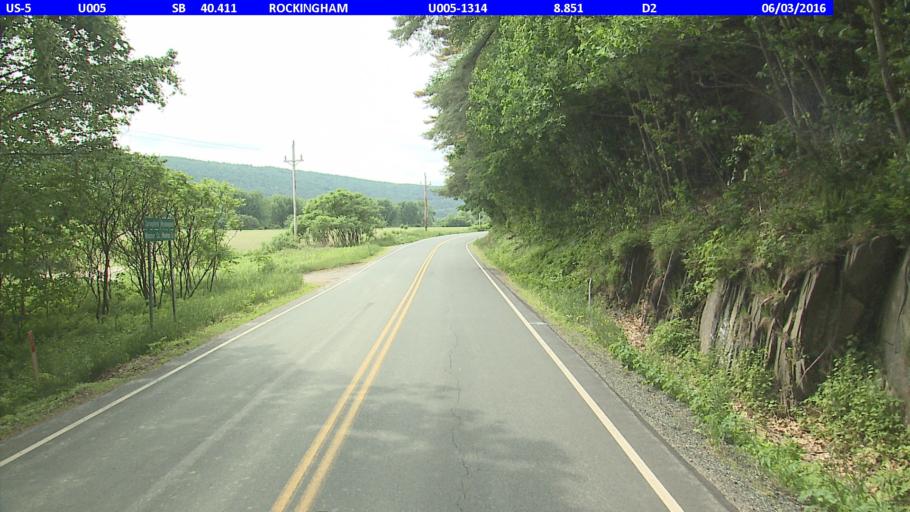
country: US
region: New Hampshire
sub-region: Sullivan County
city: Charlestown
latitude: 43.2332
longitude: -72.4382
